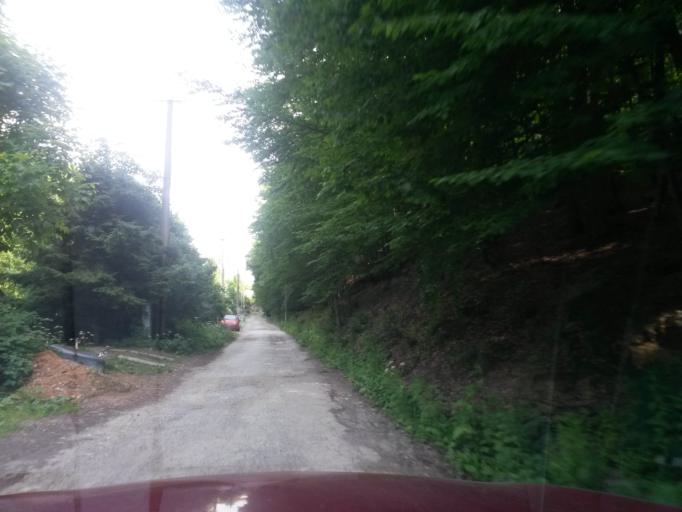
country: SK
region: Kosicky
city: Kosice
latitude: 48.7330
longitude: 21.1271
